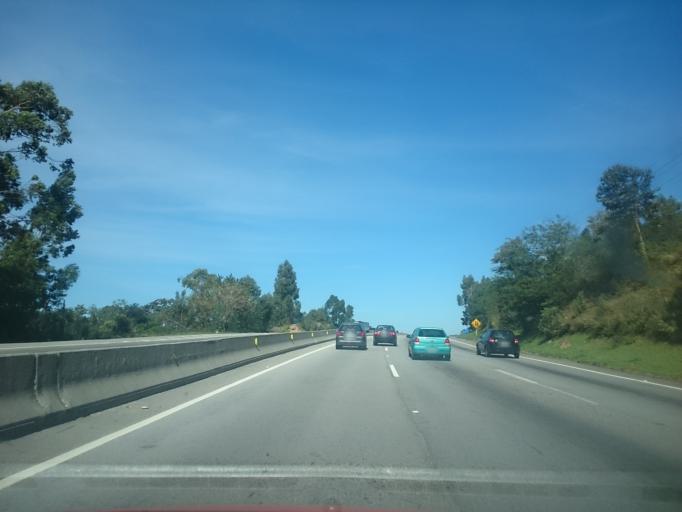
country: BR
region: Santa Catarina
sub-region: Palhoca
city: Palhoca
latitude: -27.7122
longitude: -48.6512
